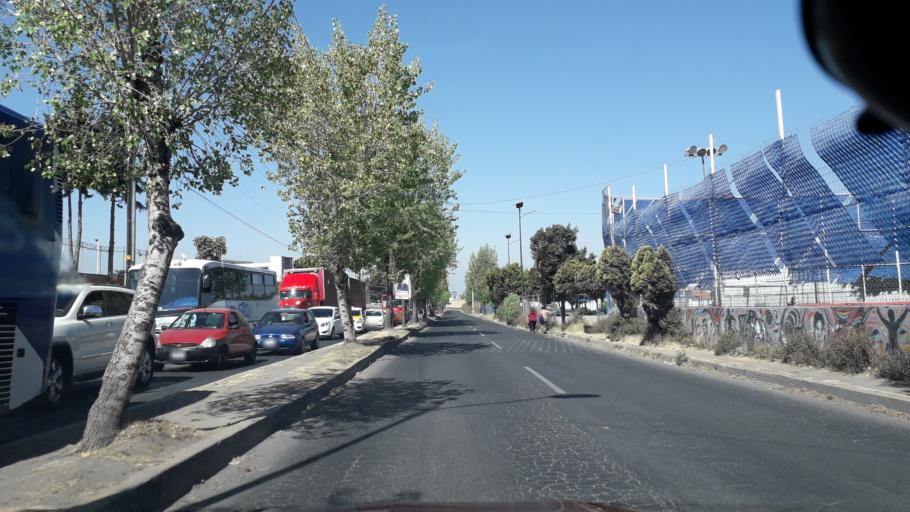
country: MX
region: Puebla
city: Puebla
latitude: 19.0809
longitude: -98.2113
